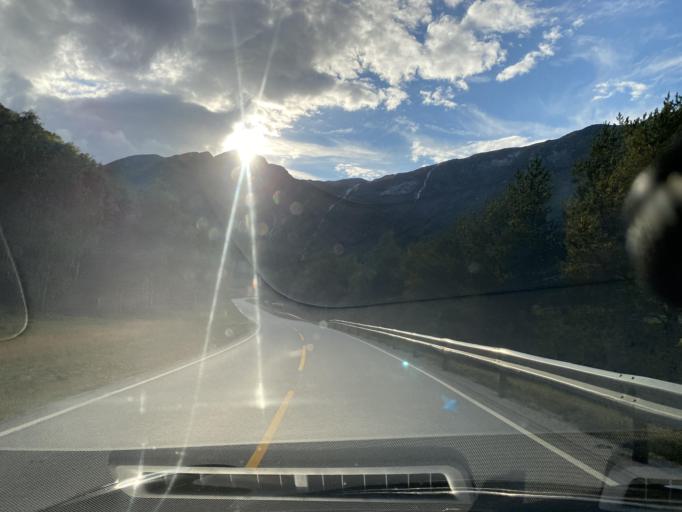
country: NO
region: Oppland
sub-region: Lom
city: Fossbergom
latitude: 61.8091
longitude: 8.4759
